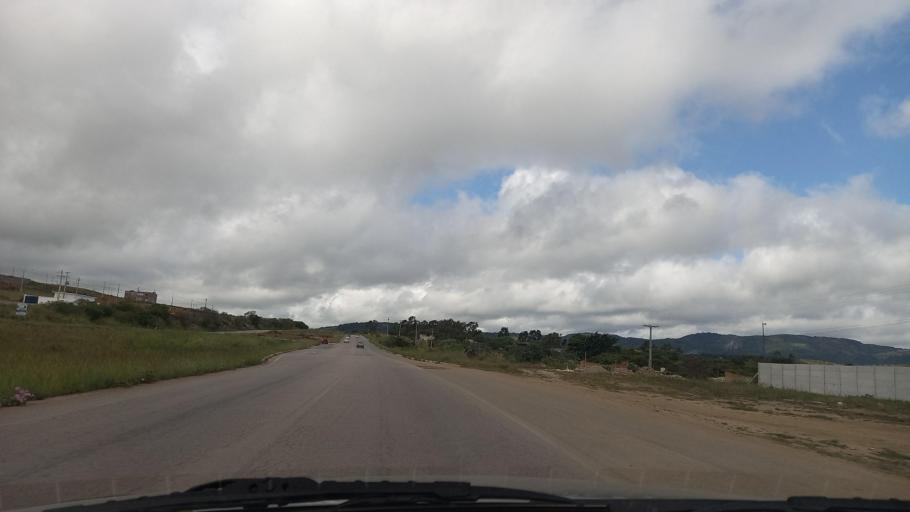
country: BR
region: Pernambuco
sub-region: Caruaru
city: Caruaru
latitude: -8.3152
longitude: -35.9914
